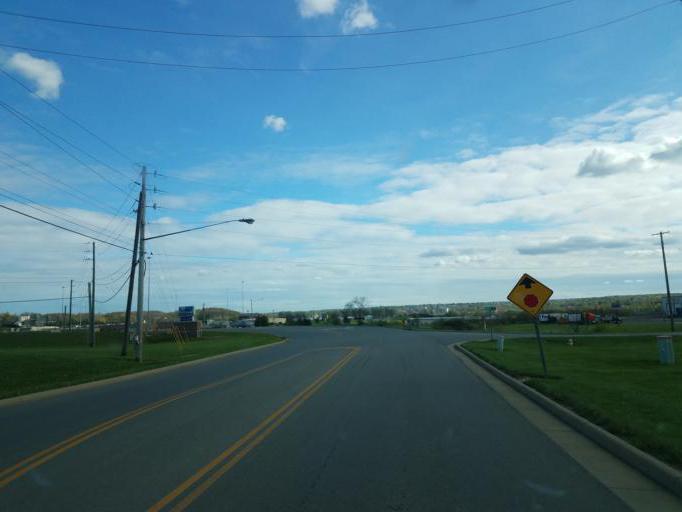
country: US
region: Ohio
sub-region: Richland County
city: Mansfield
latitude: 40.7956
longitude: -82.5135
